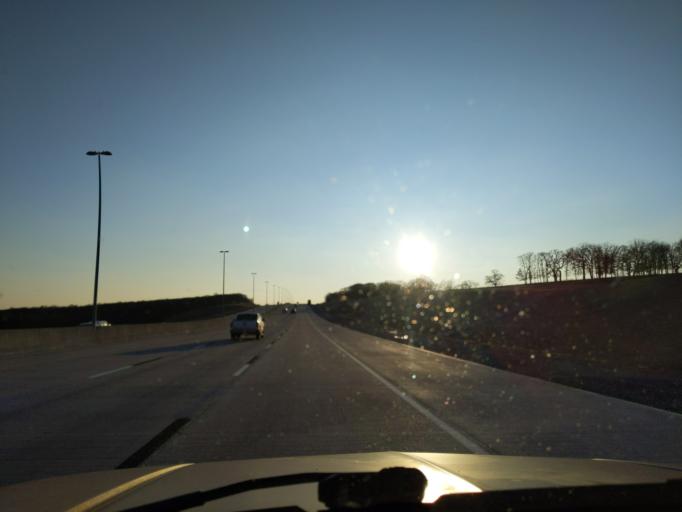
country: US
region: Oklahoma
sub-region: Creek County
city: Kellyville
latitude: 35.9363
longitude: -96.2646
